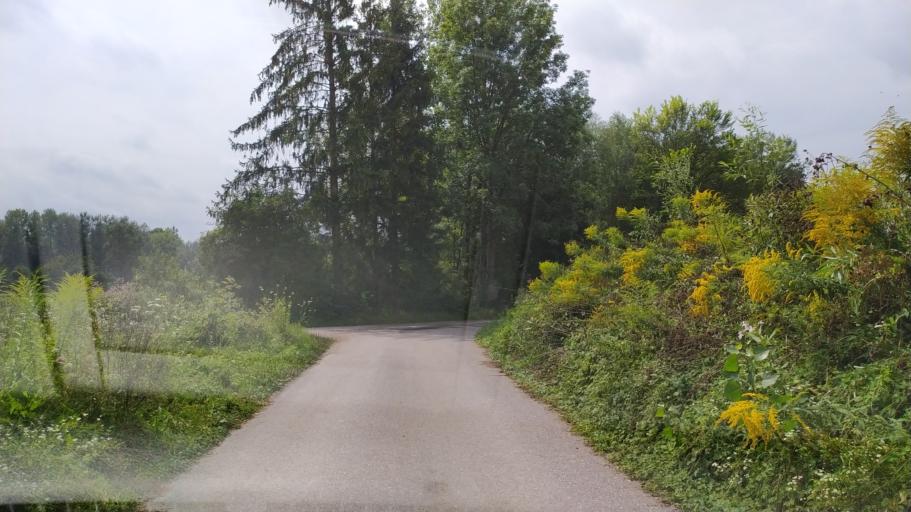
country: AT
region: Lower Austria
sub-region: Politischer Bezirk Amstetten
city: Zeillern
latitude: 48.1916
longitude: 14.7719
